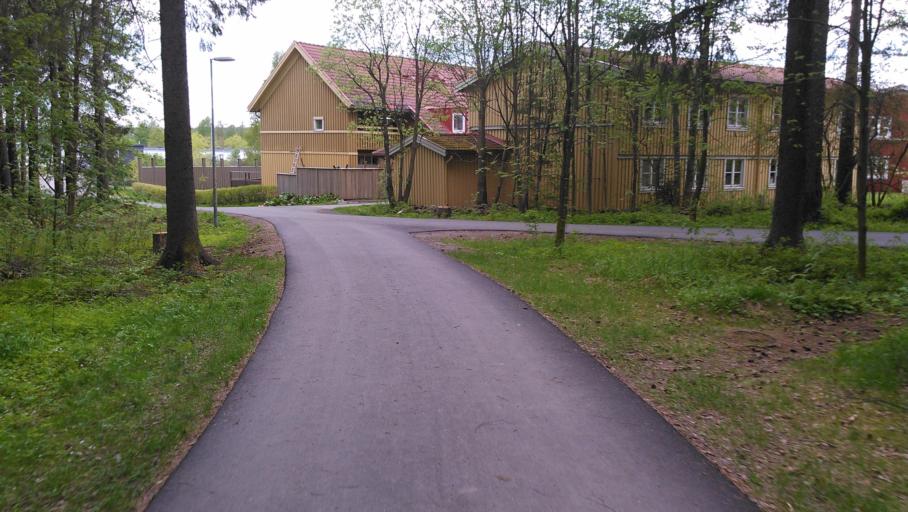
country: SE
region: Vaesterbotten
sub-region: Umea Kommun
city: Ersmark
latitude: 63.8454
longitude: 20.3157
